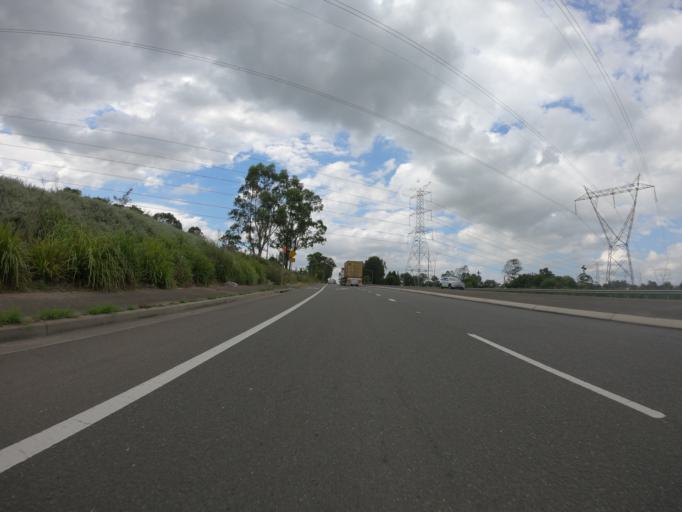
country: AU
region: New South Wales
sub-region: Blacktown
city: Mount Druitt
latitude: -33.8120
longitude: 150.7863
